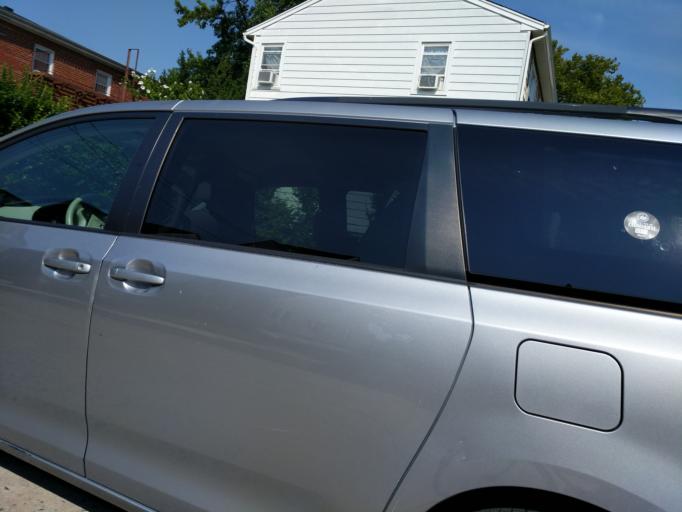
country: US
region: New York
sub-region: Nassau County
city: Hewlett
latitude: 40.6514
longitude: -73.7004
